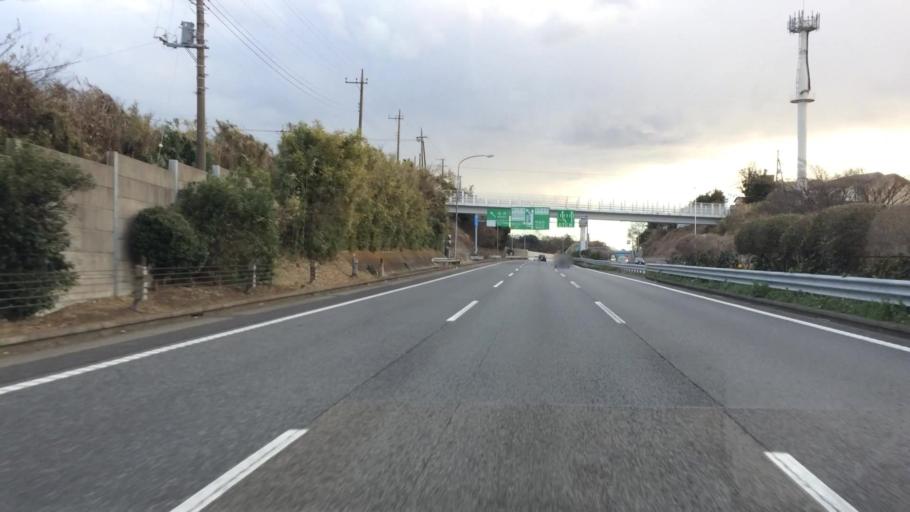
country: JP
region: Kanagawa
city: Yokohama
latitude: 35.4956
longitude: 139.5917
